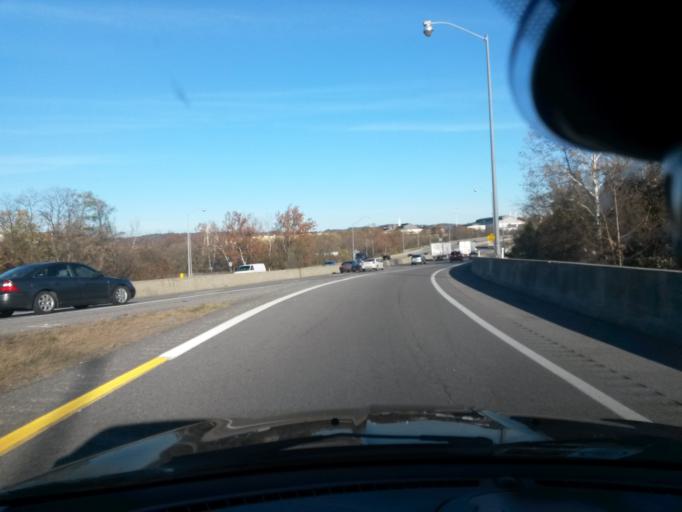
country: US
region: West Virginia
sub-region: Kanawha County
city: South Charleston
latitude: 38.3597
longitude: -81.7141
